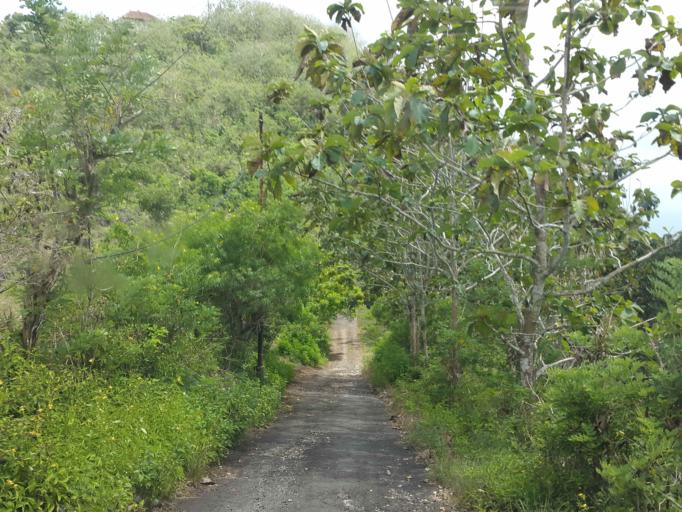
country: ID
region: Bali
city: Klumbu
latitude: -8.7322
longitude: 115.5283
